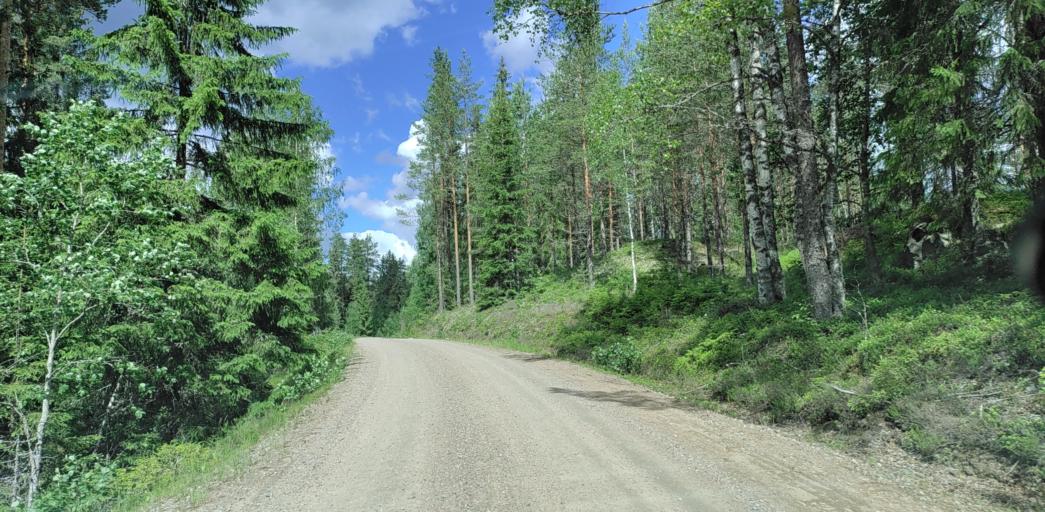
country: SE
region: Vaermland
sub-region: Hagfors Kommun
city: Ekshaerad
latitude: 60.0767
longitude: 13.2918
